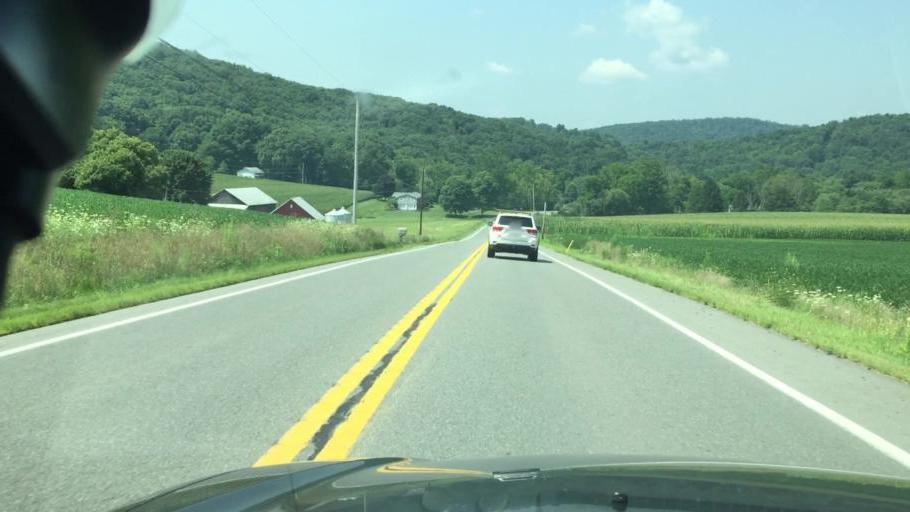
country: US
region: Pennsylvania
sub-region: Columbia County
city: Catawissa
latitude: 40.9032
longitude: -76.4990
